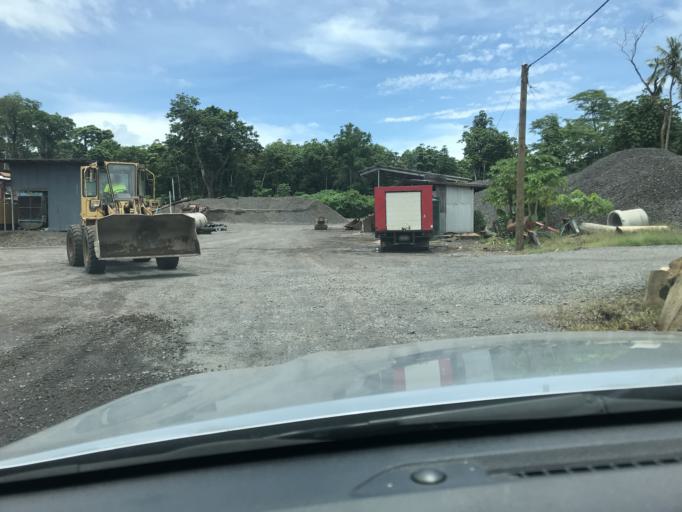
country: WS
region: Tuamasaga
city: Afenga
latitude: -13.8244
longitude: -171.8875
